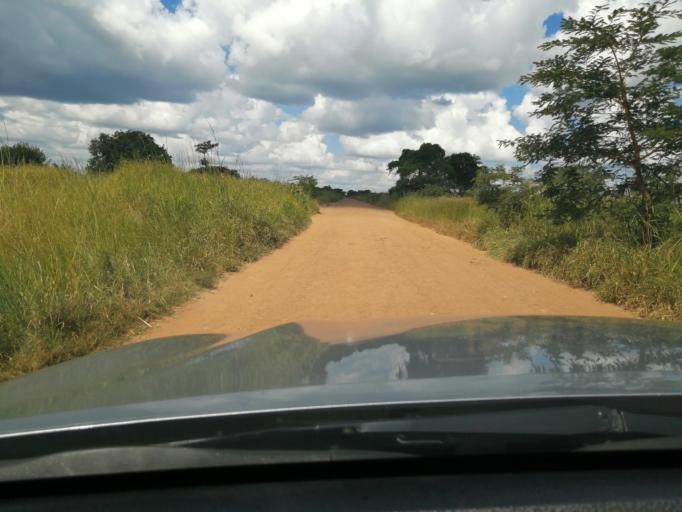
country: ZM
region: Lusaka
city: Lusaka
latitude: -15.1986
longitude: 28.0067
